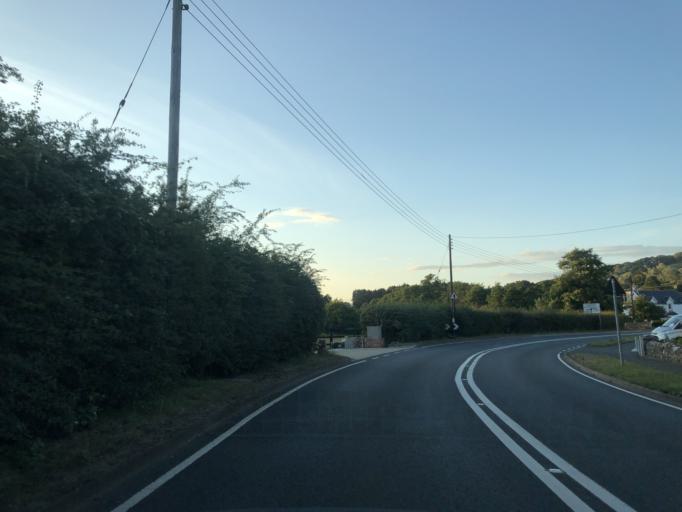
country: GB
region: England
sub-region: Isle of Wight
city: Newport
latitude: 50.6735
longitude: -1.2853
